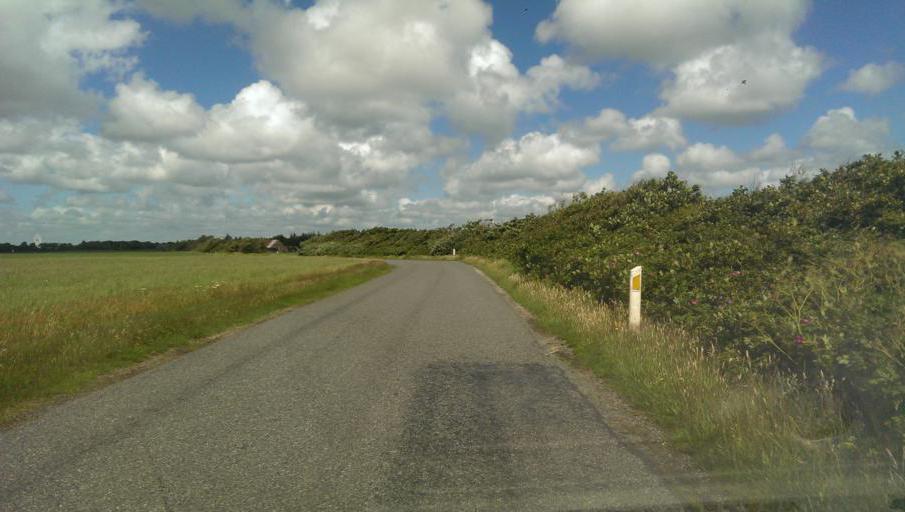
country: DK
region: Central Jutland
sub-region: Holstebro Kommune
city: Ulfborg
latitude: 56.2532
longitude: 8.2360
